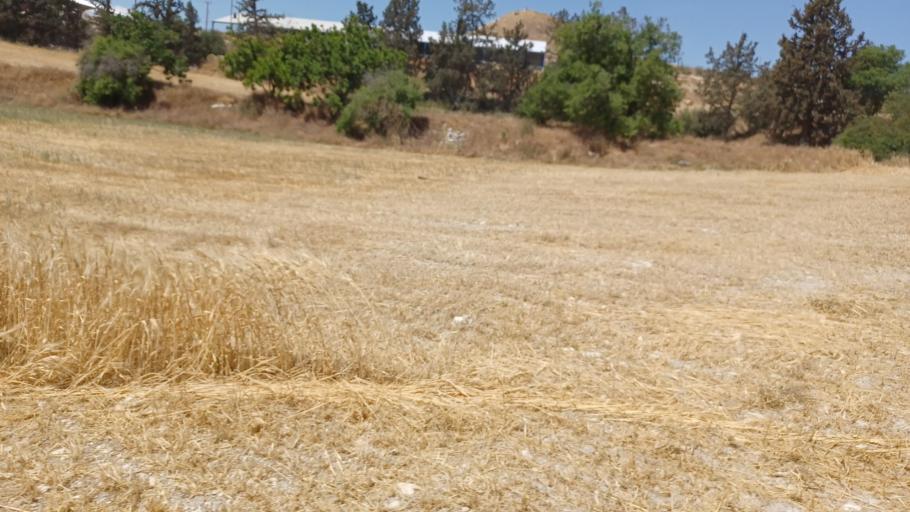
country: CY
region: Larnaka
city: Athienou
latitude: 35.0341
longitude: 33.5401
